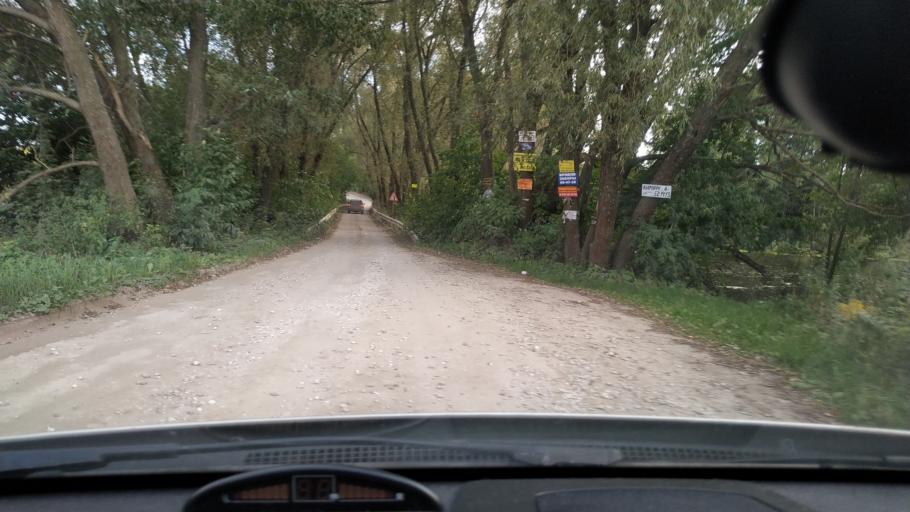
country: RU
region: Rjazan
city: Polyany
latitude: 54.5626
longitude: 39.8748
